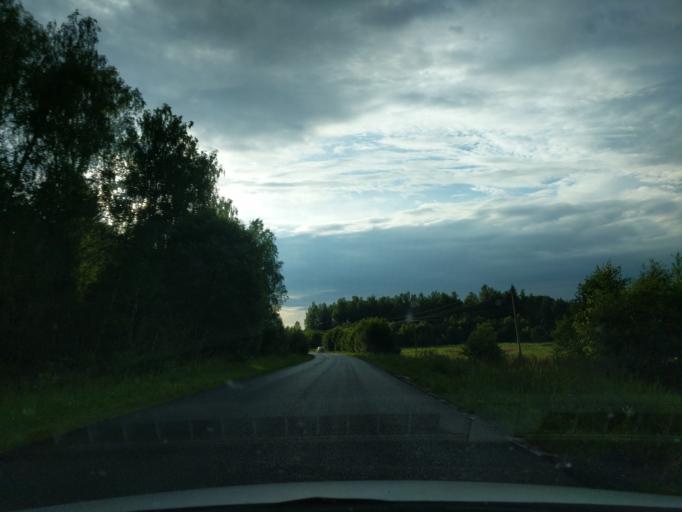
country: RU
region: Kaluga
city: Myatlevo
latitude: 54.8040
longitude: 35.7049
